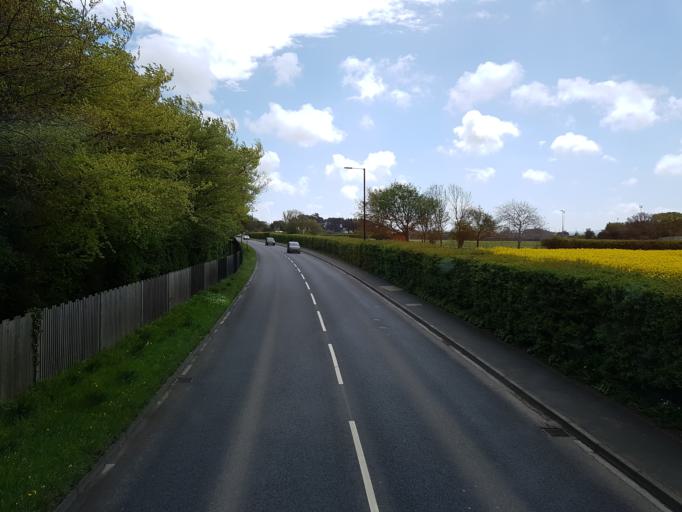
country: GB
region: England
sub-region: Isle of Wight
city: East Cowes
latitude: 50.7476
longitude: -1.2756
